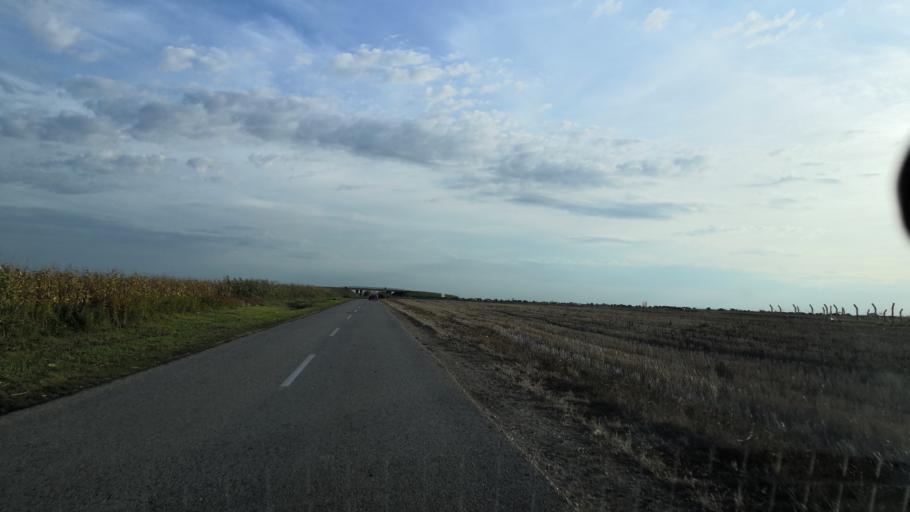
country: RS
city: Novi Karlovci
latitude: 45.0523
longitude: 20.1775
